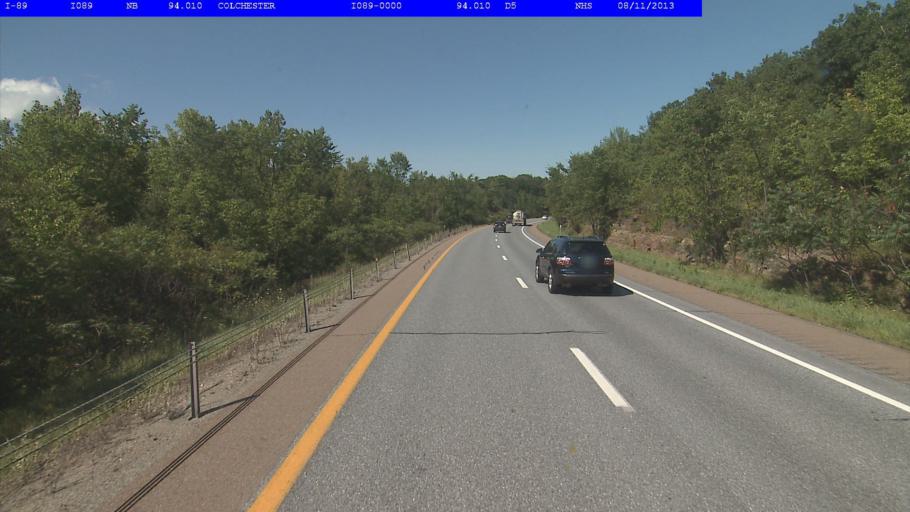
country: US
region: Vermont
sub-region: Chittenden County
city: Winooski
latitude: 44.5382
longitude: -73.1975
